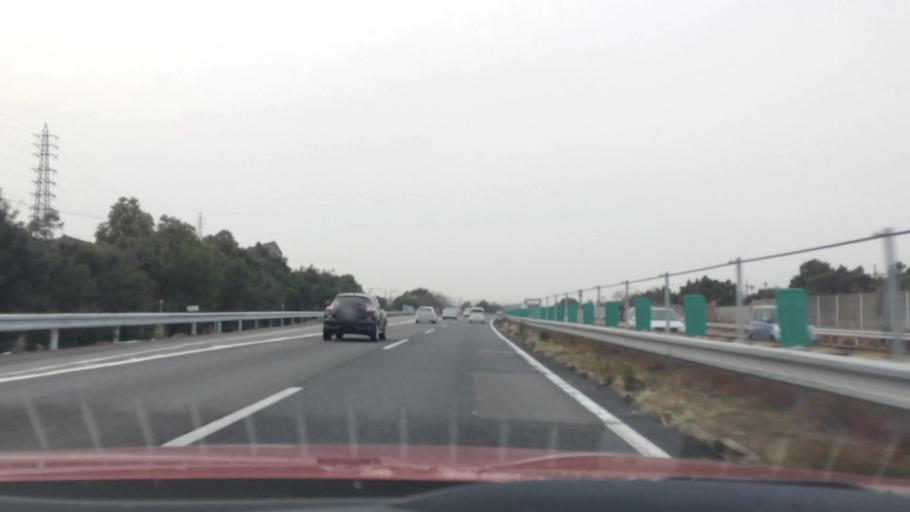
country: JP
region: Aichi
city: Sobue
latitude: 35.2872
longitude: 136.7446
